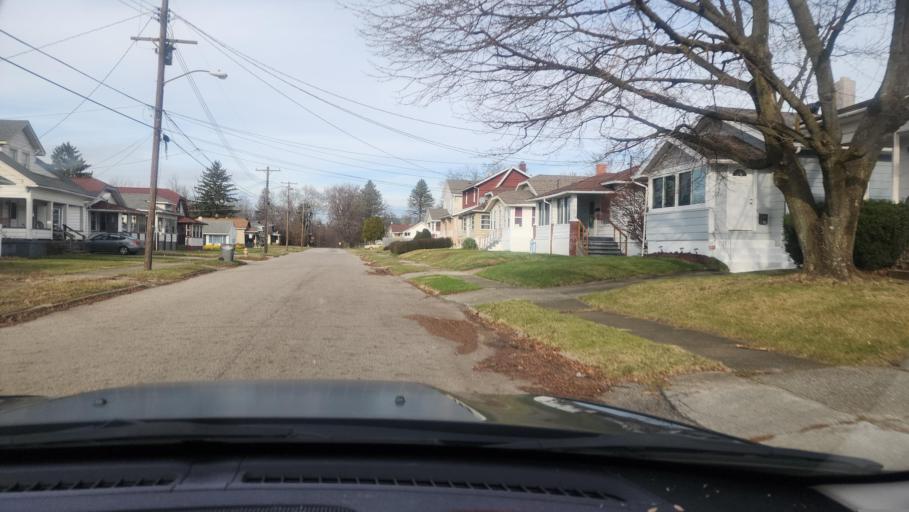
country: US
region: Ohio
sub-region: Mahoning County
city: Campbell
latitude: 41.0973
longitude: -80.6186
